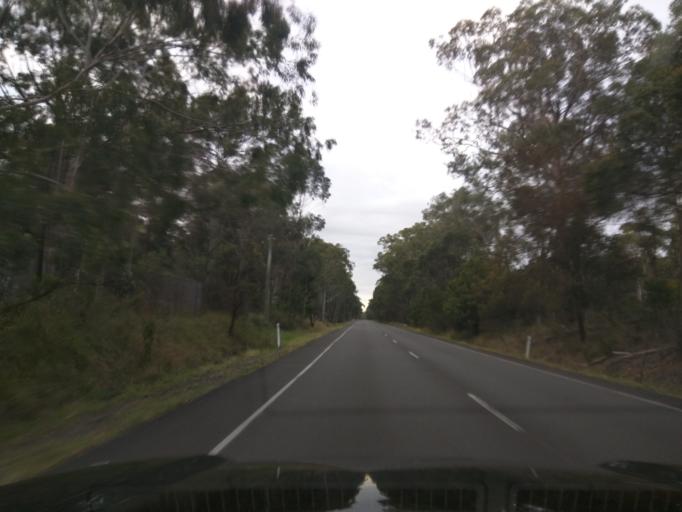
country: AU
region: New South Wales
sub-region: Wollondilly
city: Douglas Park
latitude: -34.2521
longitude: 150.7245
